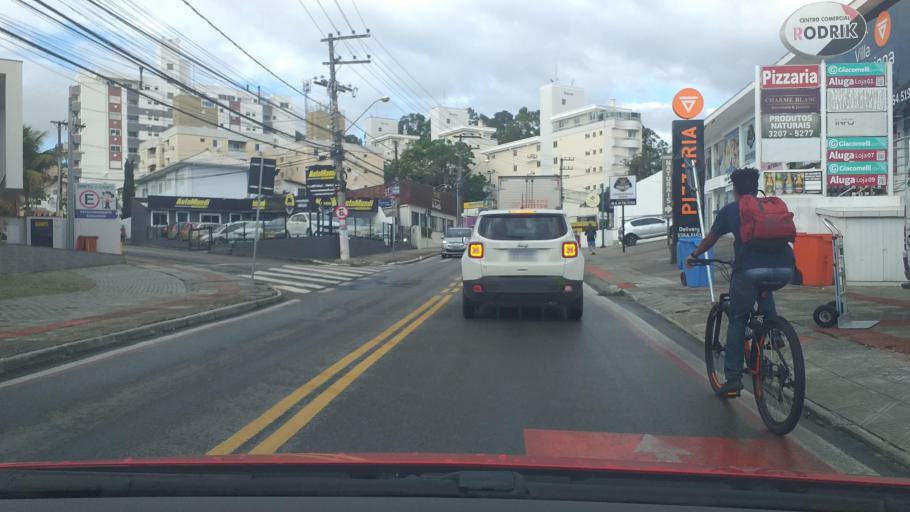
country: BR
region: Santa Catarina
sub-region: Florianopolis
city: Corrego Grande
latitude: -27.6003
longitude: -48.5128
